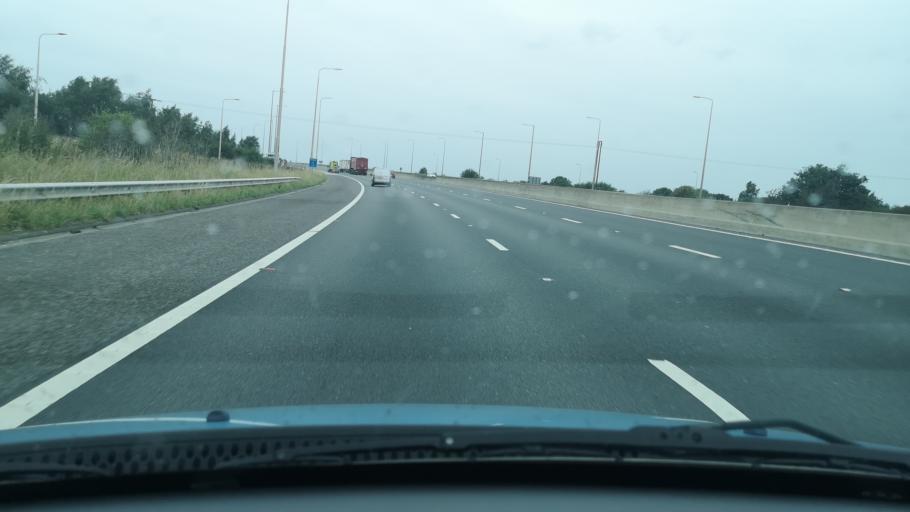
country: GB
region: England
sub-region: Doncaster
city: Hatfield
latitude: 53.5905
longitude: -0.9645
